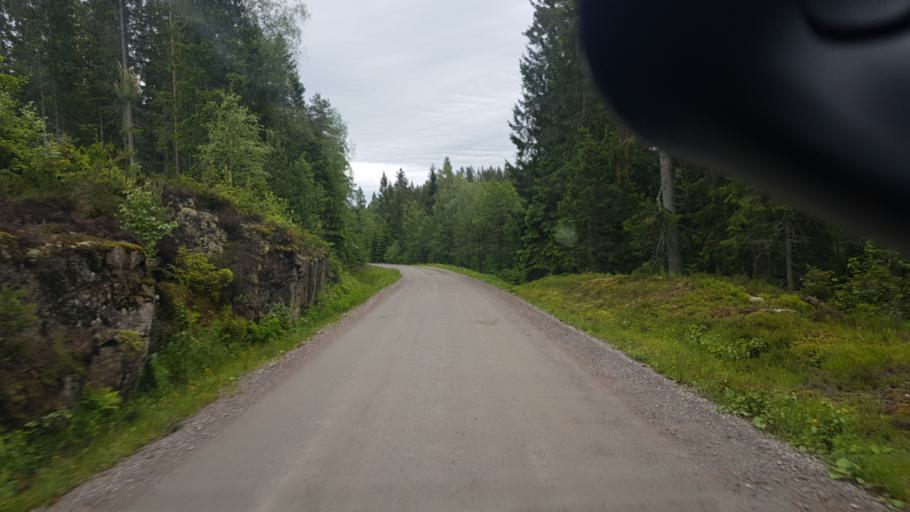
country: NO
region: Ostfold
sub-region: Romskog
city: Romskog
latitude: 59.7105
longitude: 12.0371
